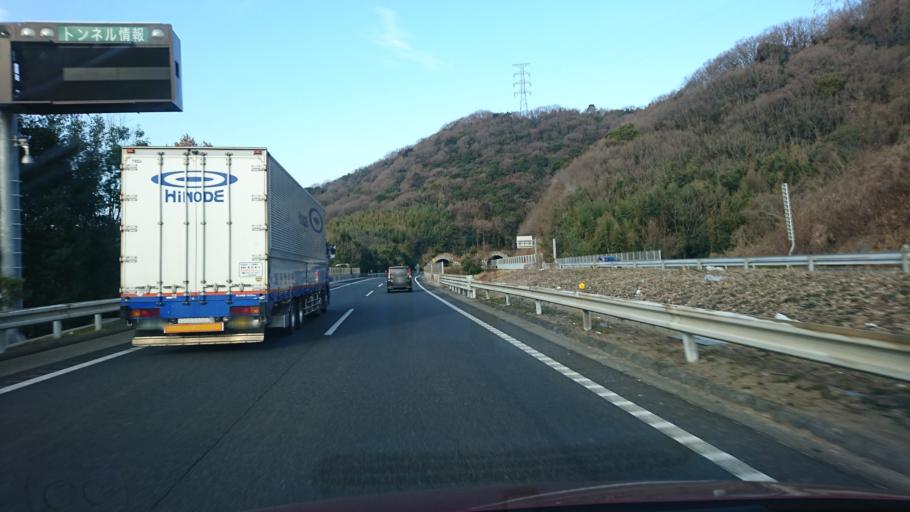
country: JP
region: Hyogo
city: Himeji
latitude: 34.8523
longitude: 134.7349
